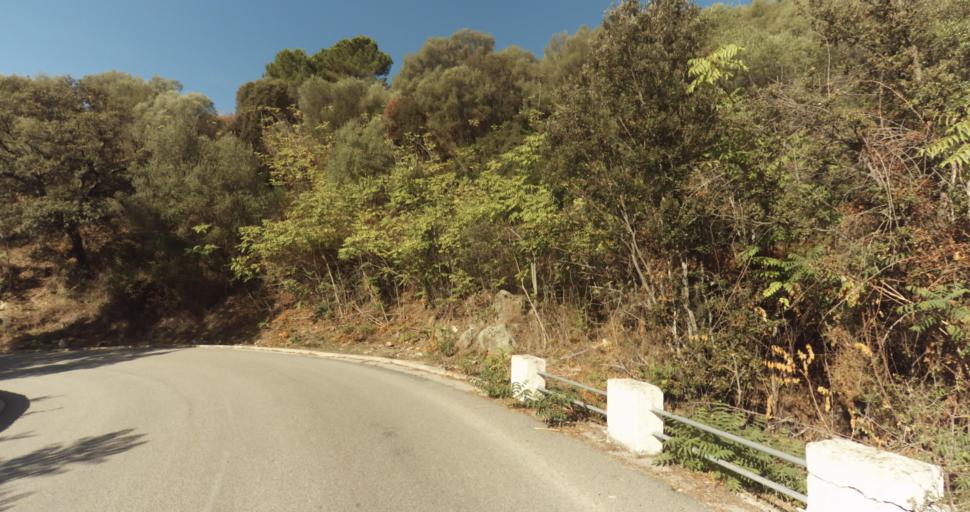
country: FR
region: Corsica
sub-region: Departement de la Corse-du-Sud
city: Ajaccio
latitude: 41.9328
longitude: 8.7038
